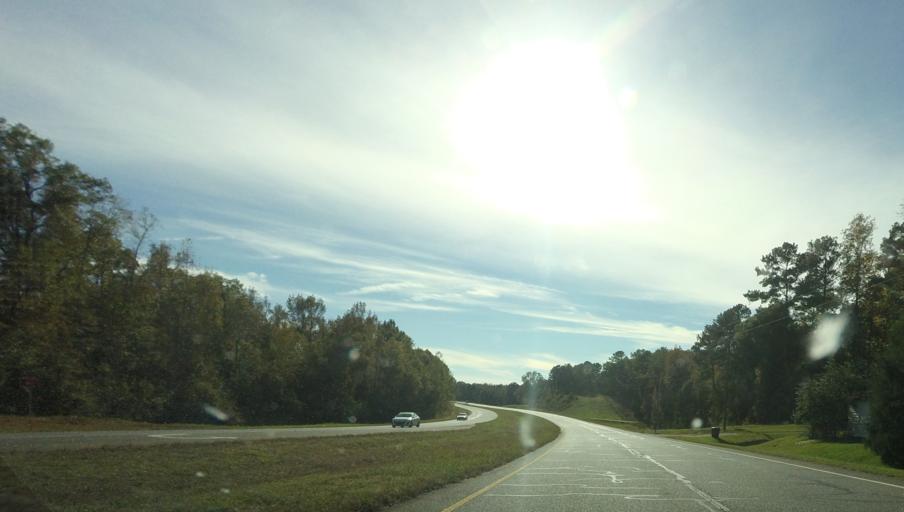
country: US
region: Georgia
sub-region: Taylor County
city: Butler
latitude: 32.7317
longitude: -84.2275
